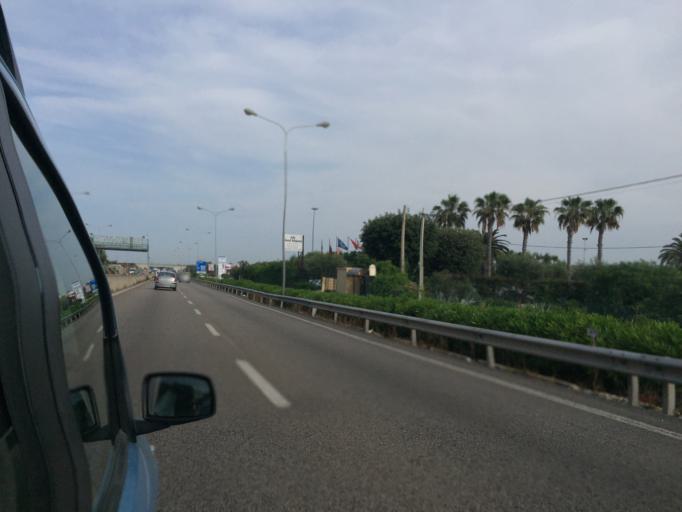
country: IT
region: Apulia
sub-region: Provincia di Bari
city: Triggiano
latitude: 41.0985
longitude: 16.9357
